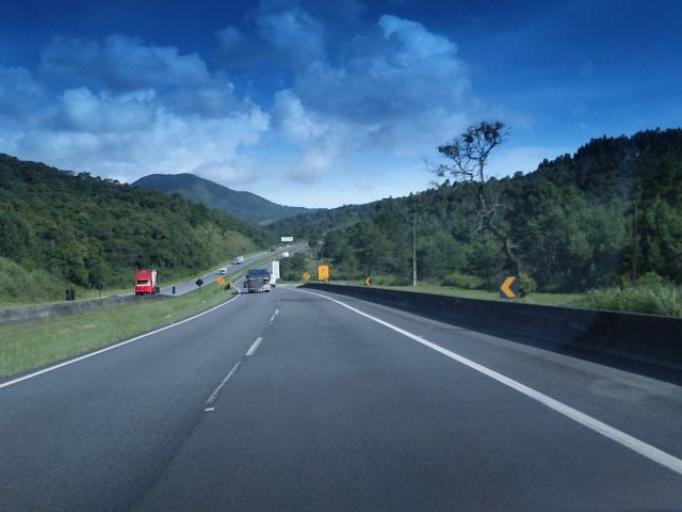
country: BR
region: Parana
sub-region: Campina Grande Do Sul
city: Campina Grande do Sul
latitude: -25.2386
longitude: -48.9063
